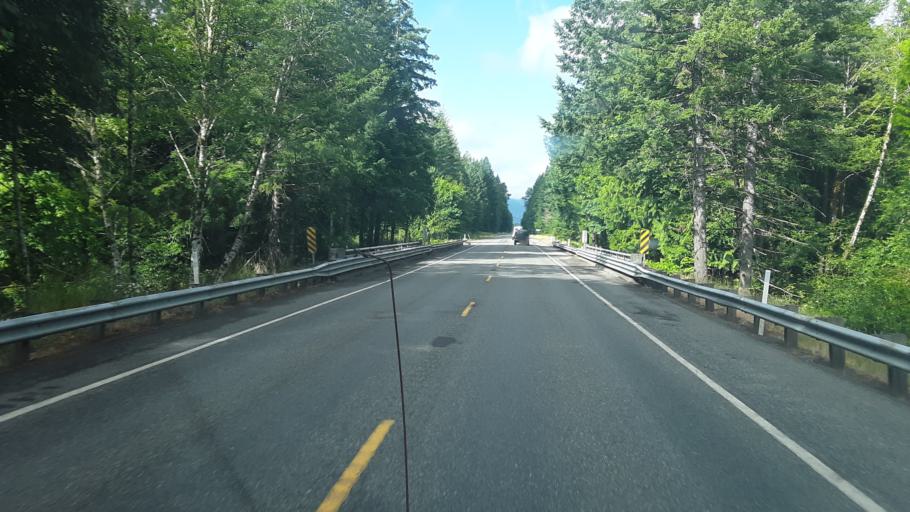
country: US
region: Washington
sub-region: Lewis County
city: Morton
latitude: 46.5689
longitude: -121.7044
